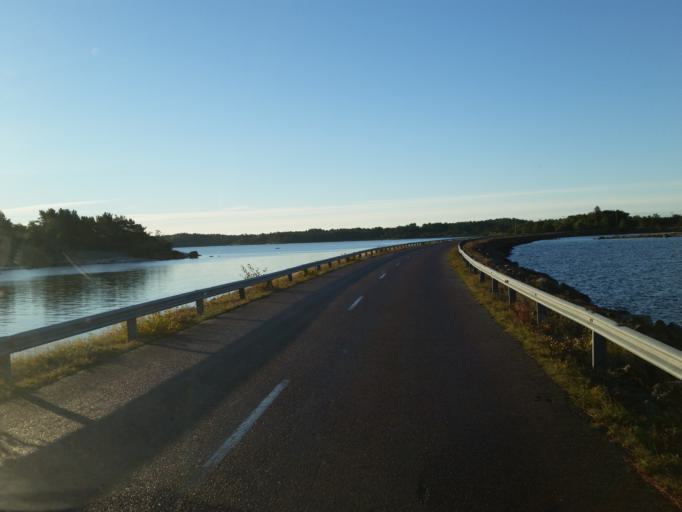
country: AX
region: Alands skaergard
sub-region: Vardoe
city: Vardoe
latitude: 60.3187
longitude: 20.3750
